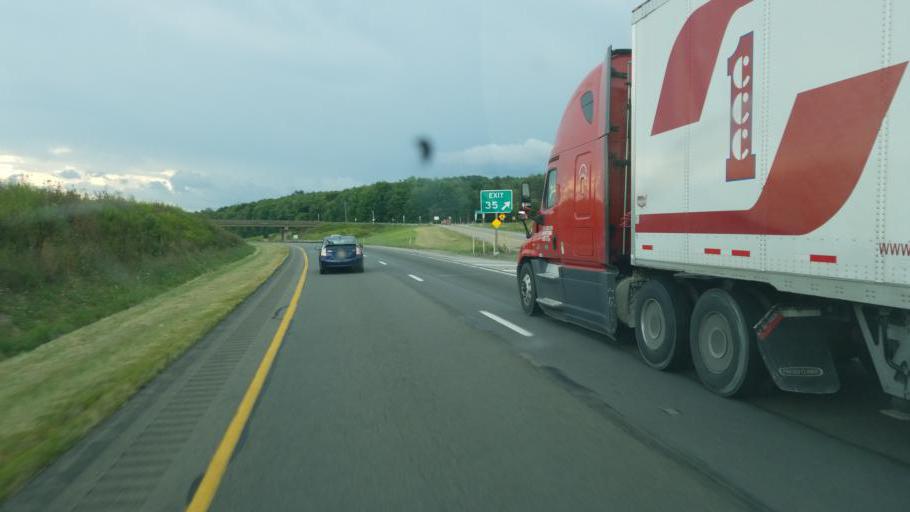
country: US
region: Pennsylvania
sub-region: Venango County
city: Franklin
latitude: 41.1903
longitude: -79.8718
